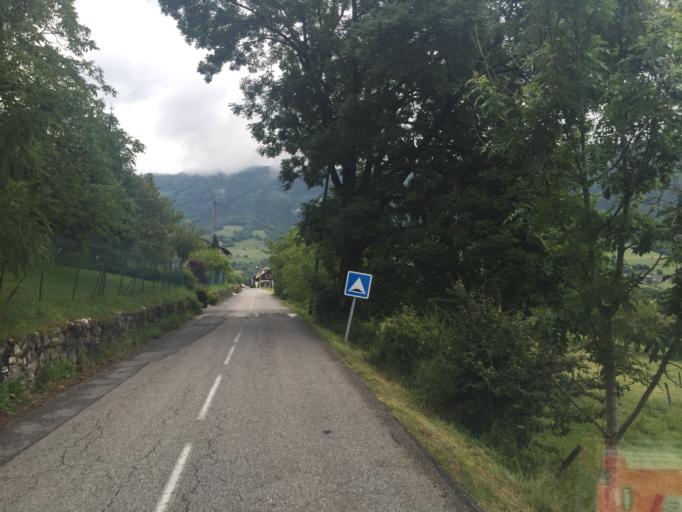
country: FR
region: Rhone-Alpes
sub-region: Departement de la Savoie
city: Barby
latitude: 45.5870
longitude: 6.0100
